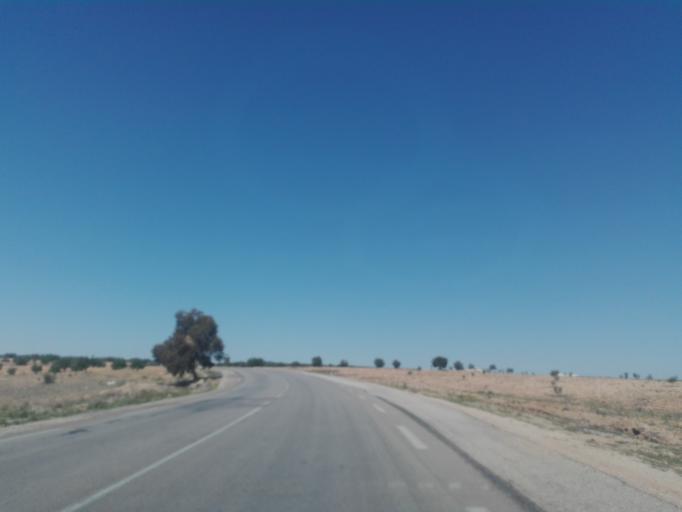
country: TN
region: Safaqis
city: Bi'r `Ali Bin Khalifah
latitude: 34.7460
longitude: 10.3610
